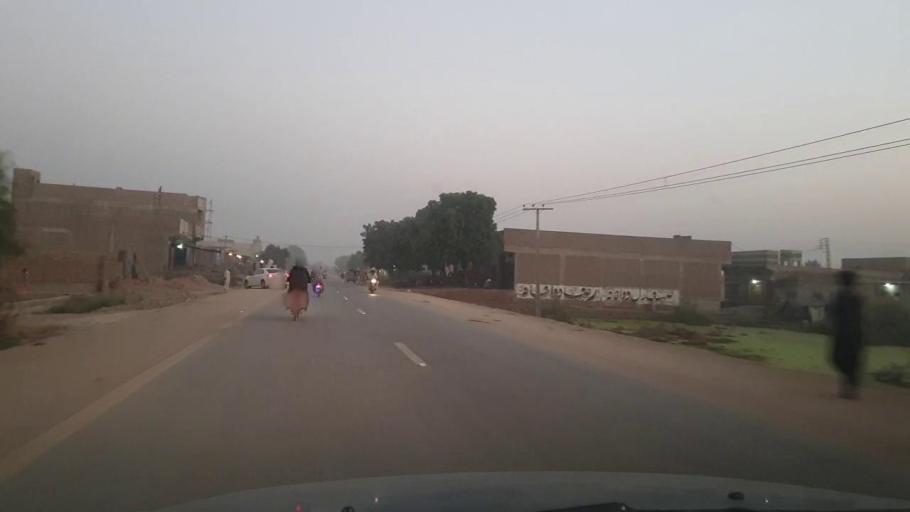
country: PK
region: Sindh
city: Tando Allahyar
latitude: 25.4490
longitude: 68.7279
